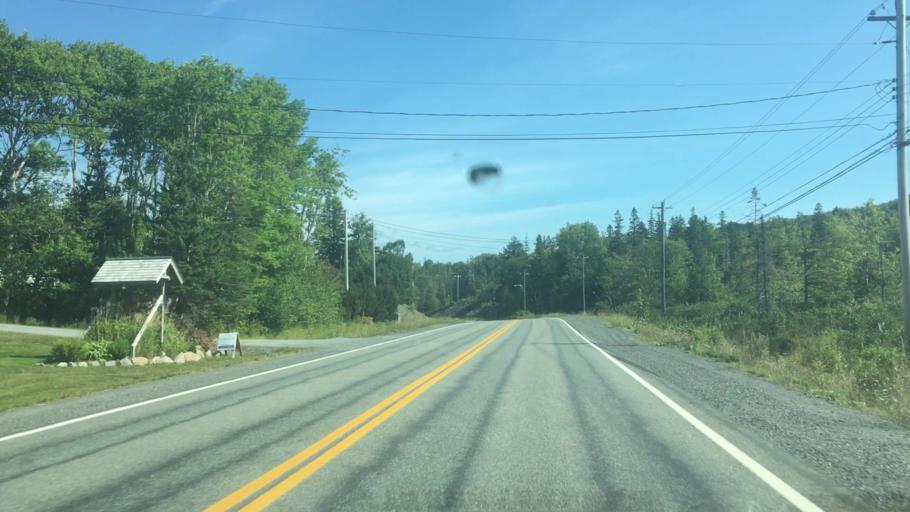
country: CA
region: Nova Scotia
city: Sydney
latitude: 45.9963
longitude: -60.4055
